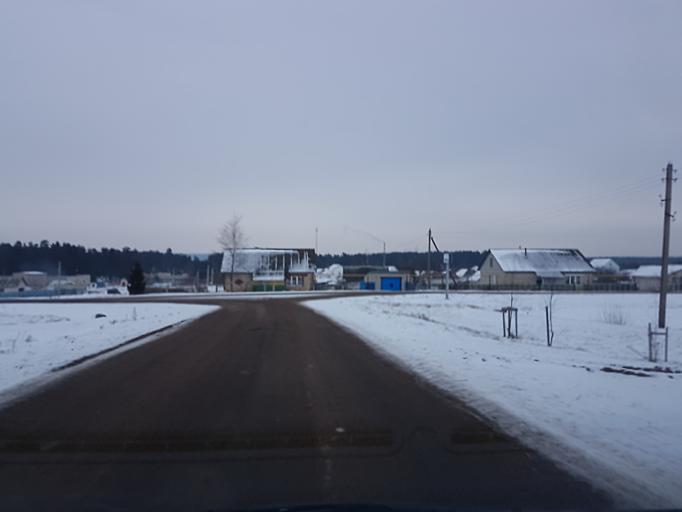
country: BY
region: Minsk
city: Rakaw
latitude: 53.9567
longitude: 27.0461
